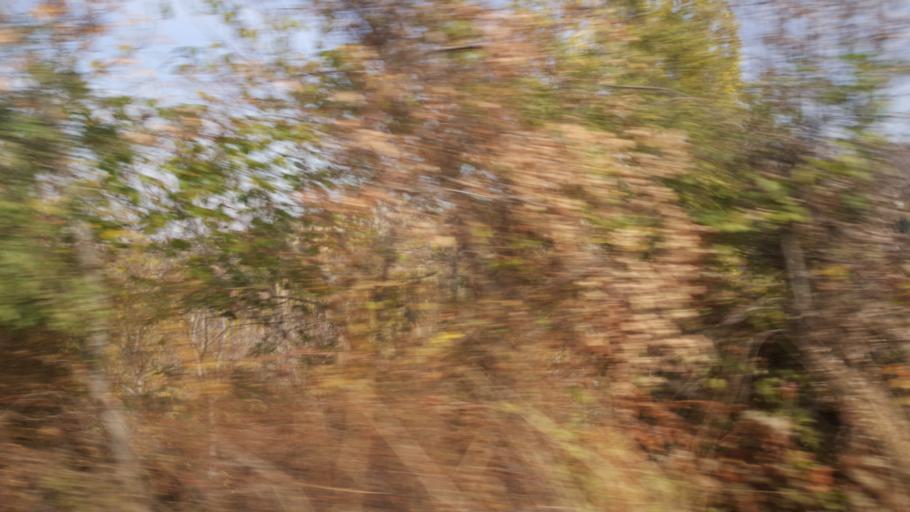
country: TR
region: Eskisehir
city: Mihaliccik
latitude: 39.9785
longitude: 31.3665
